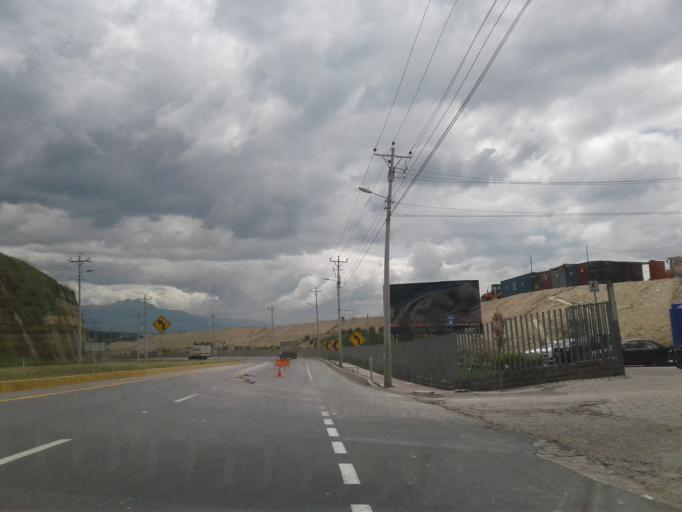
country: EC
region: Pichincha
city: Sangolqui
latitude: -0.2951
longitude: -78.3559
